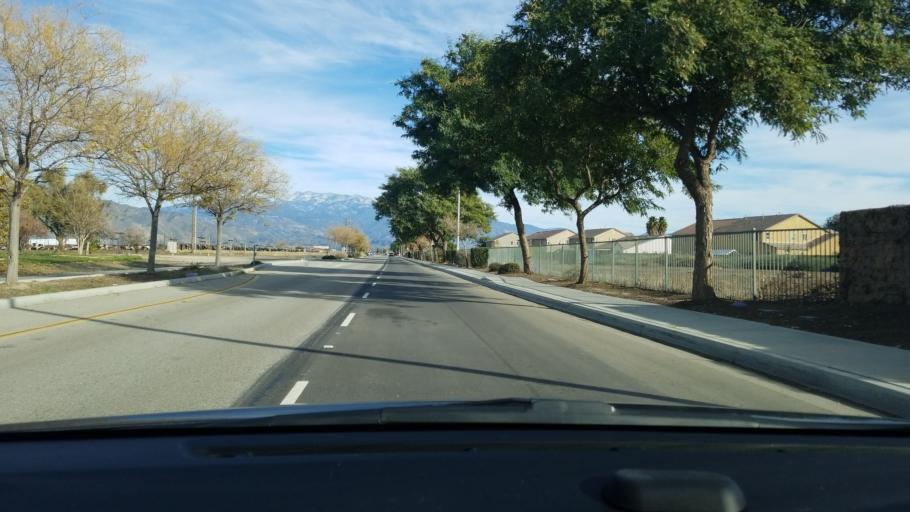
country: US
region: California
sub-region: Riverside County
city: Hemet
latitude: 33.7873
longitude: -117.0229
